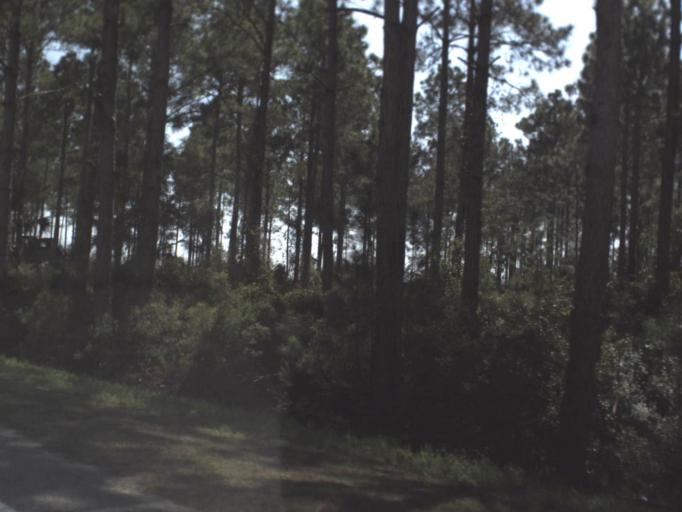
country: US
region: Florida
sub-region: Gulf County
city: Port Saint Joe
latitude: 29.7788
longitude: -85.2989
